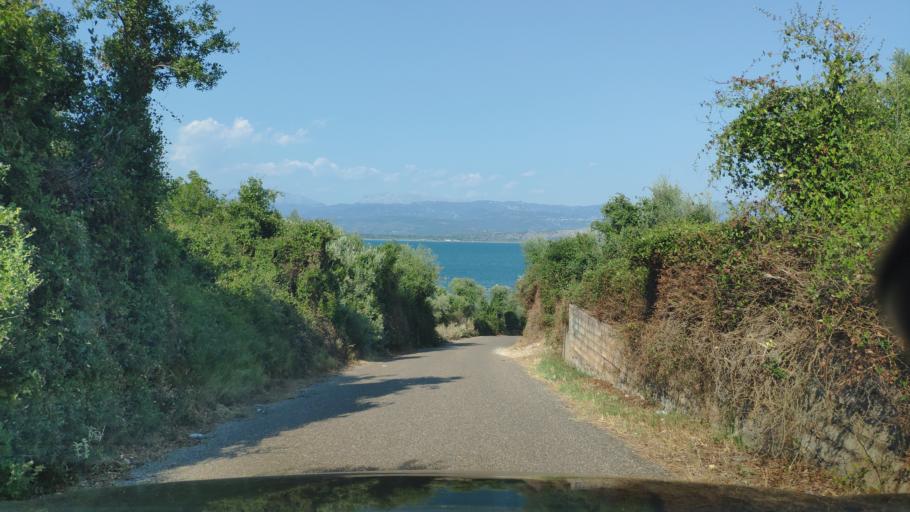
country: GR
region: West Greece
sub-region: Nomos Aitolias kai Akarnanias
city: Amfilochia
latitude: 38.9041
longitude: 21.1134
